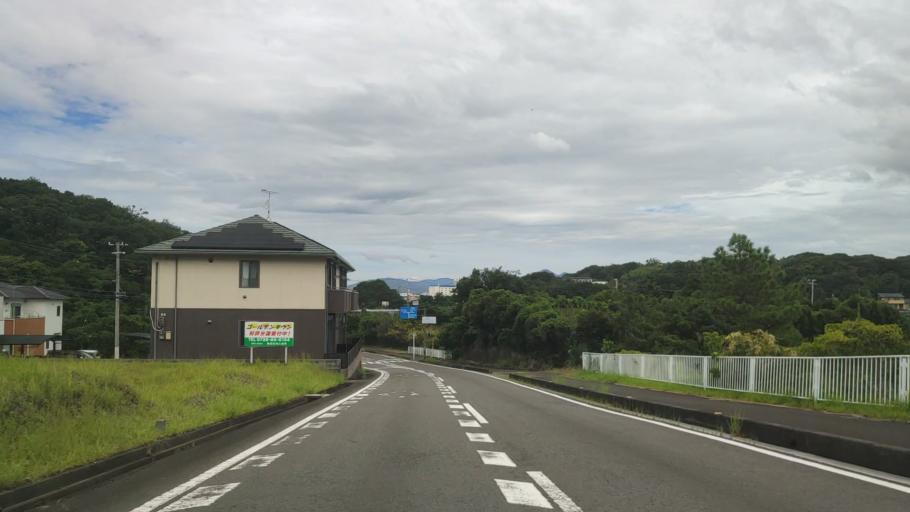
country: JP
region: Wakayama
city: Tanabe
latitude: 33.6897
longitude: 135.3881
